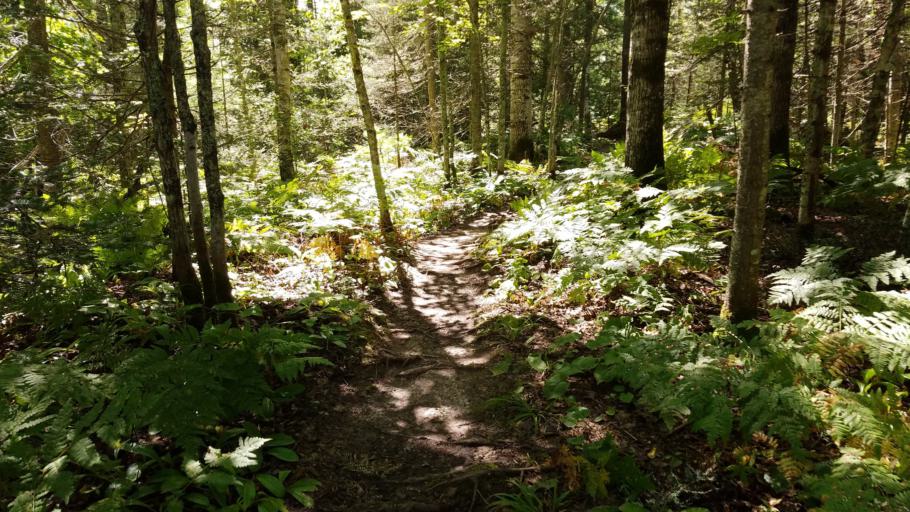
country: US
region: Michigan
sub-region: Ontonagon County
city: Ontonagon
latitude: 46.6501
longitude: -89.1660
